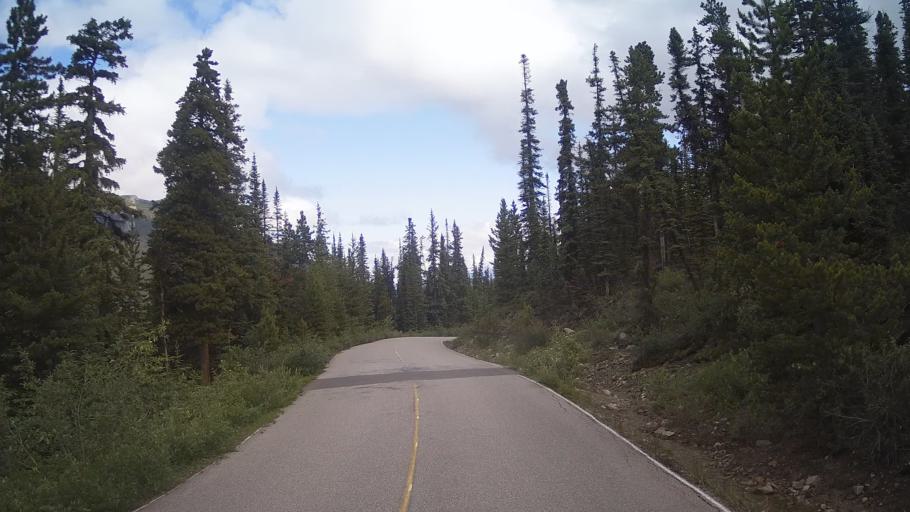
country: CA
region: Alberta
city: Jasper Park Lodge
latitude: 52.7104
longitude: -118.0562
